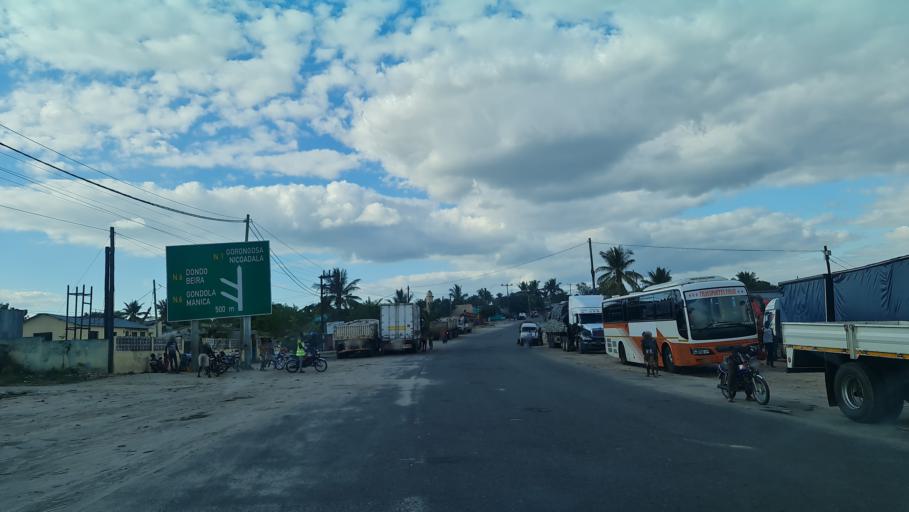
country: MZ
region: Manica
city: Chimoio
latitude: -19.2121
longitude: 33.9245
